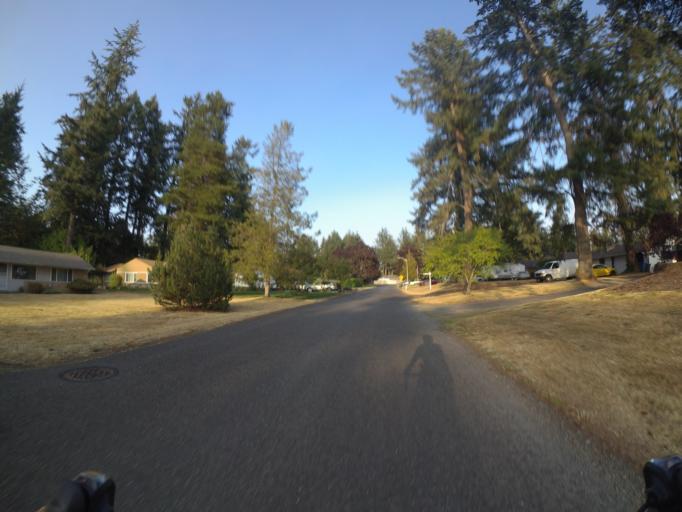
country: US
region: Washington
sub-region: Pierce County
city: Lakewood
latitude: 47.1489
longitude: -122.5174
